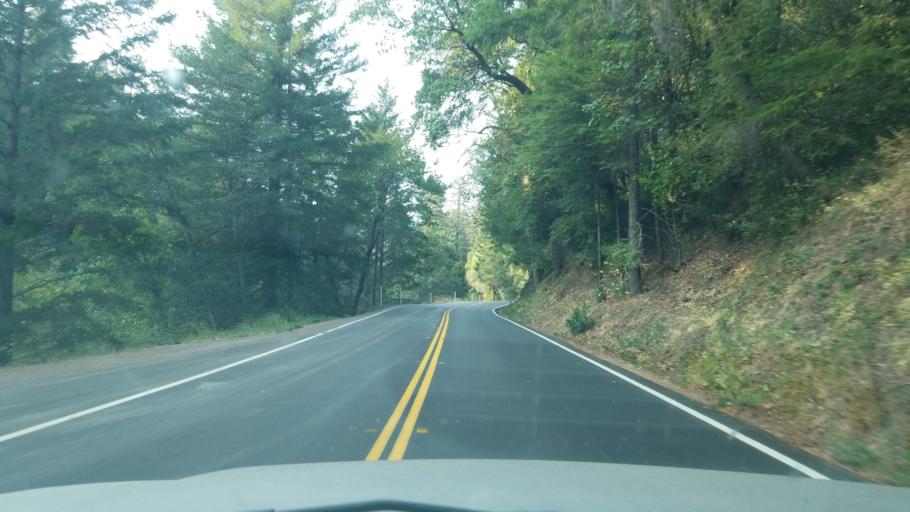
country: US
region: California
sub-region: Humboldt County
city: Redway
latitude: 40.2736
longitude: -123.8508
